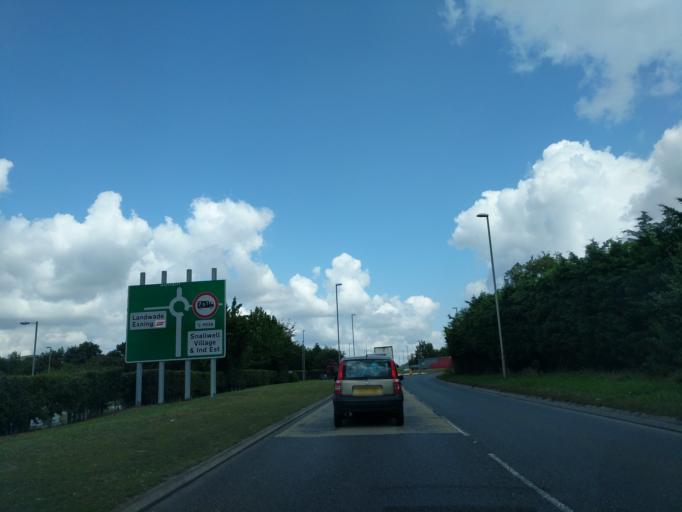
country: GB
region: England
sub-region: Suffolk
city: Exning
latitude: 52.2900
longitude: 0.3918
